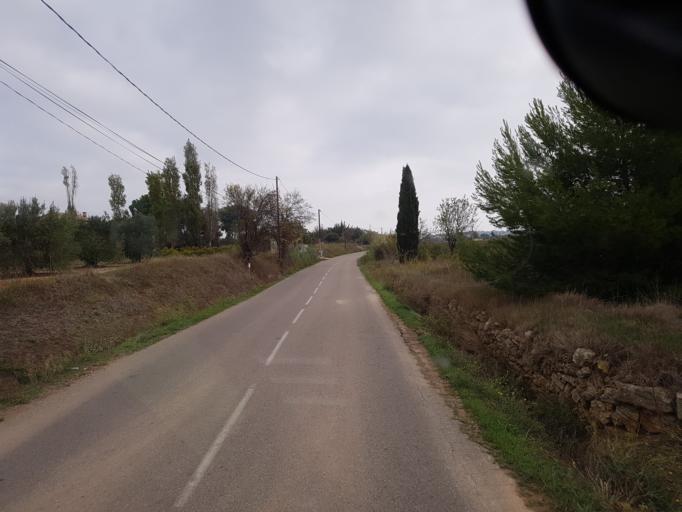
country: FR
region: Languedoc-Roussillon
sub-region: Departement de l'Herault
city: Loupian
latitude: 43.4461
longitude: 3.5859
